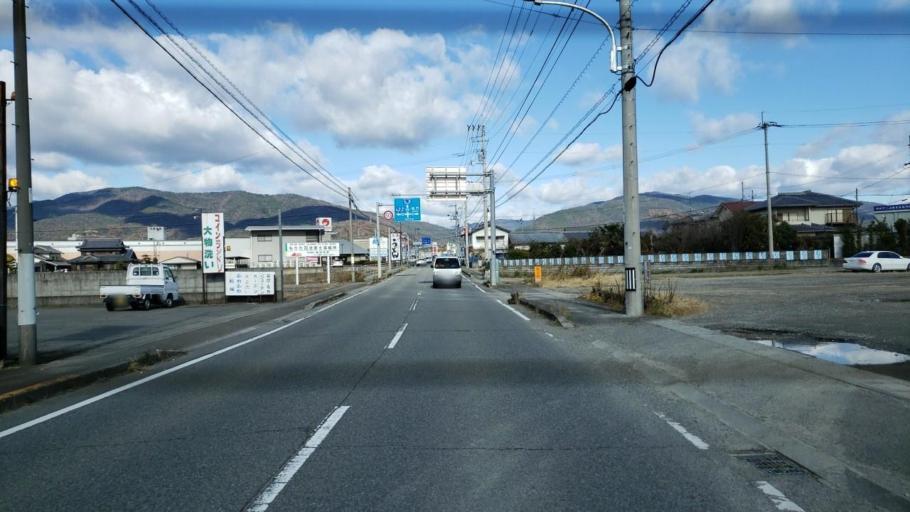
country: JP
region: Tokushima
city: Kamojimacho-jogejima
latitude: 34.0990
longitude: 134.3450
